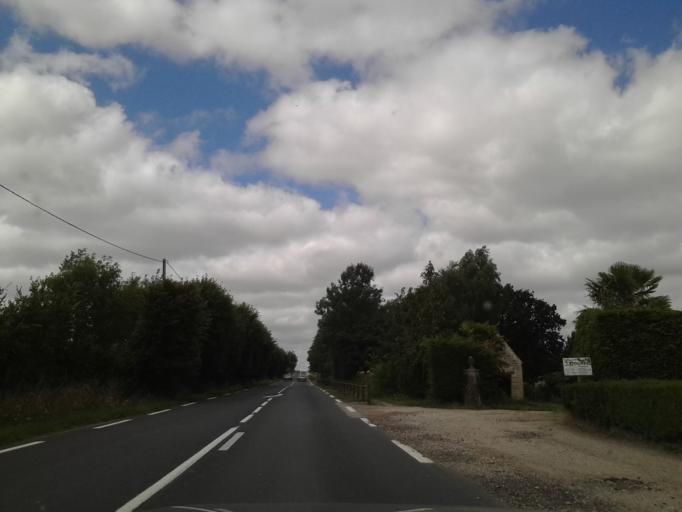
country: FR
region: Lower Normandy
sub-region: Departement de la Manche
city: Valognes
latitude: 49.5167
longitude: -1.4893
